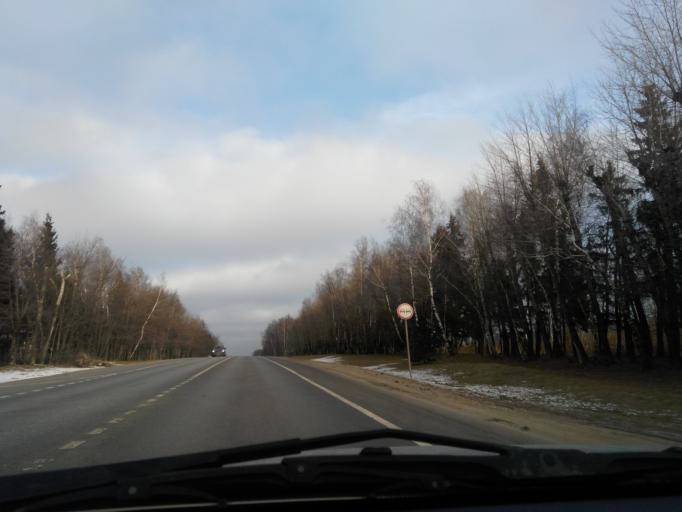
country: RU
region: Moskovskaya
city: Aprelevka
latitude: 55.2819
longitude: 37.1193
